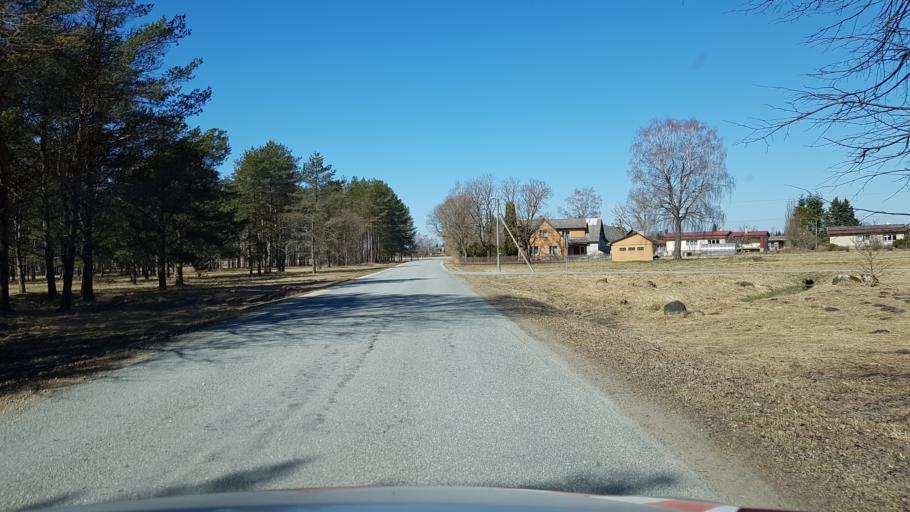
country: EE
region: Laeaene-Virumaa
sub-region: Rakke vald
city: Rakke
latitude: 59.0464
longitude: 26.3980
